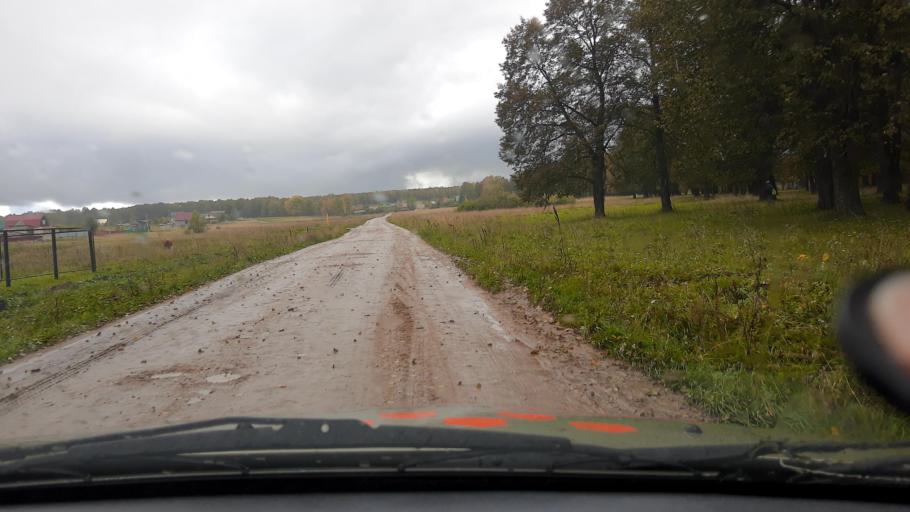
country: RU
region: Bashkortostan
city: Kudeyevskiy
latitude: 54.8800
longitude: 56.6323
